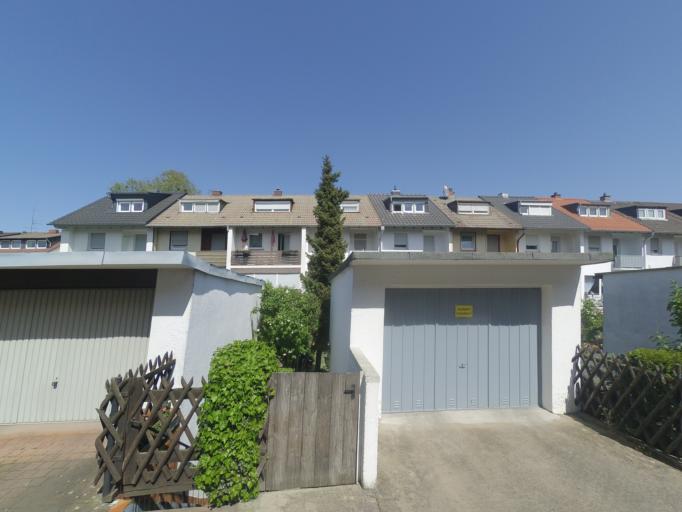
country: DE
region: Rheinland-Pfalz
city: Ludwigshafen am Rhein
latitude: 49.4696
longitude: 8.4309
